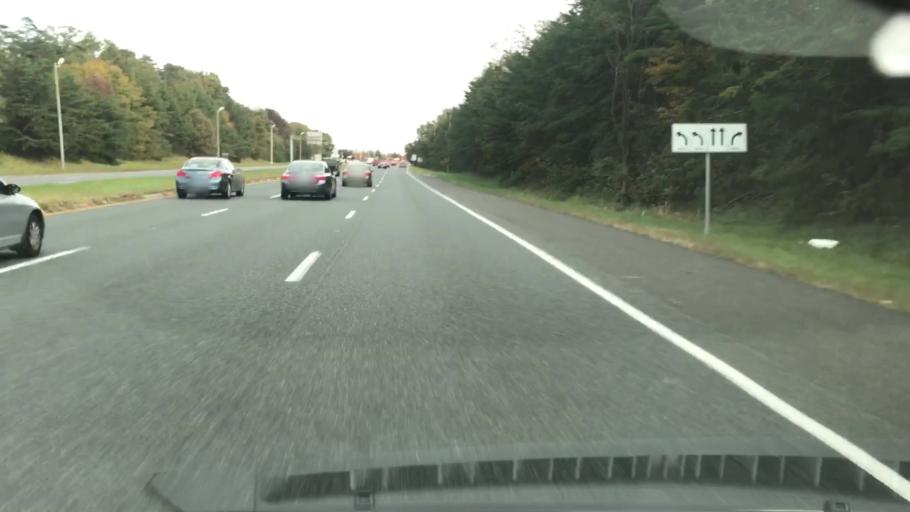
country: US
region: Virginia
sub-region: Fairfax County
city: Franconia
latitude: 38.7664
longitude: -77.1611
